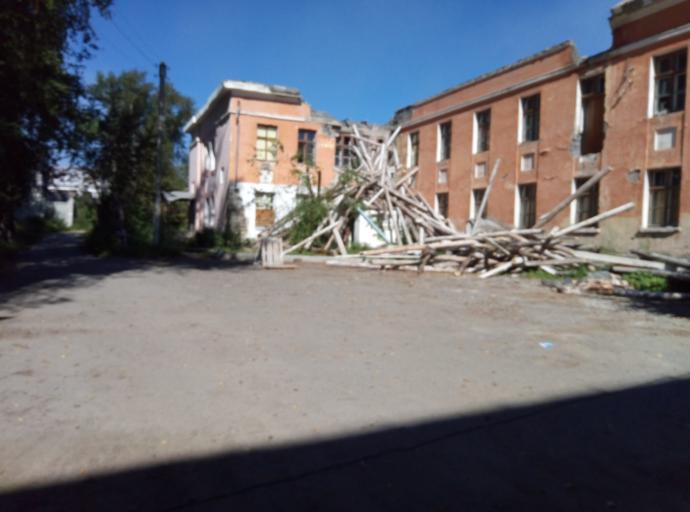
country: RU
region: Sverdlovsk
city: Krasnotur'insk
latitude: 59.7651
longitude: 60.1794
